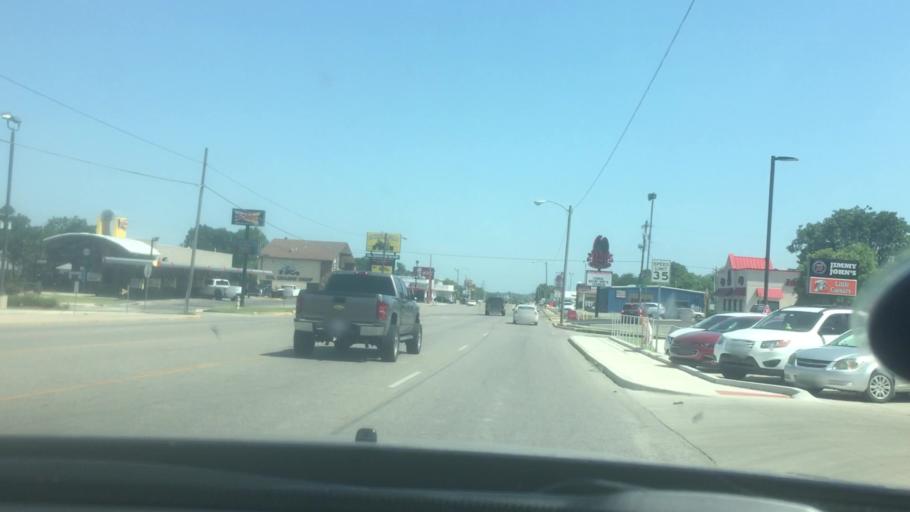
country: US
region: Oklahoma
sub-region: Pontotoc County
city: Ada
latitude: 34.7772
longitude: -96.6699
